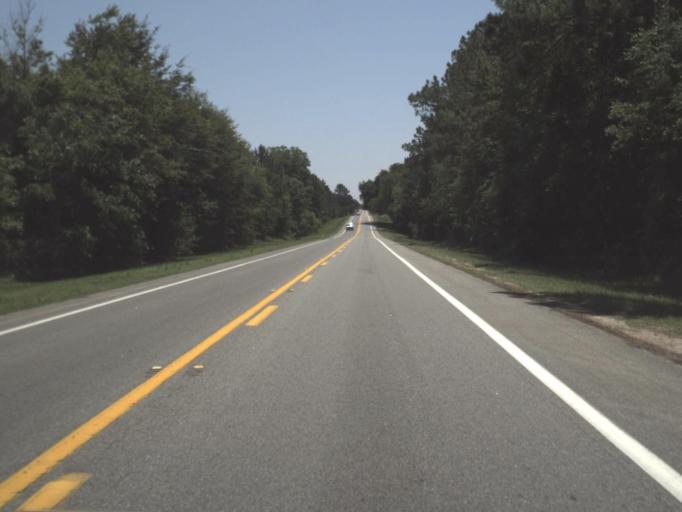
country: US
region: Florida
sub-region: Suwannee County
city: Live Oak
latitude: 30.3253
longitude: -83.0498
